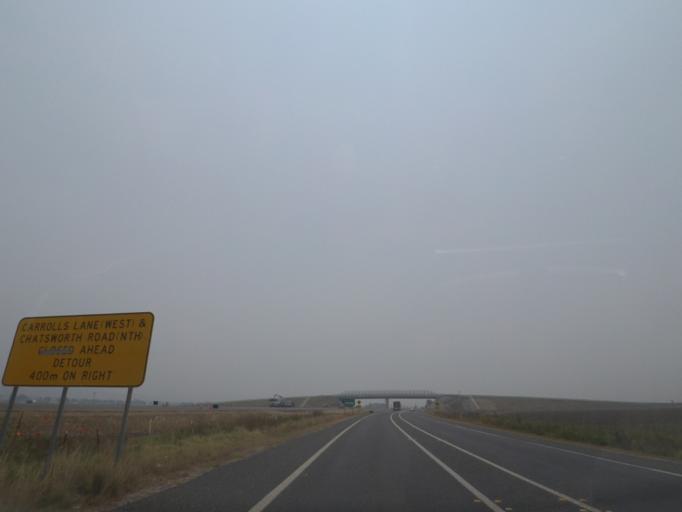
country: AU
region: New South Wales
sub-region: Clarence Valley
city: Maclean
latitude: -29.3953
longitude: 153.2392
